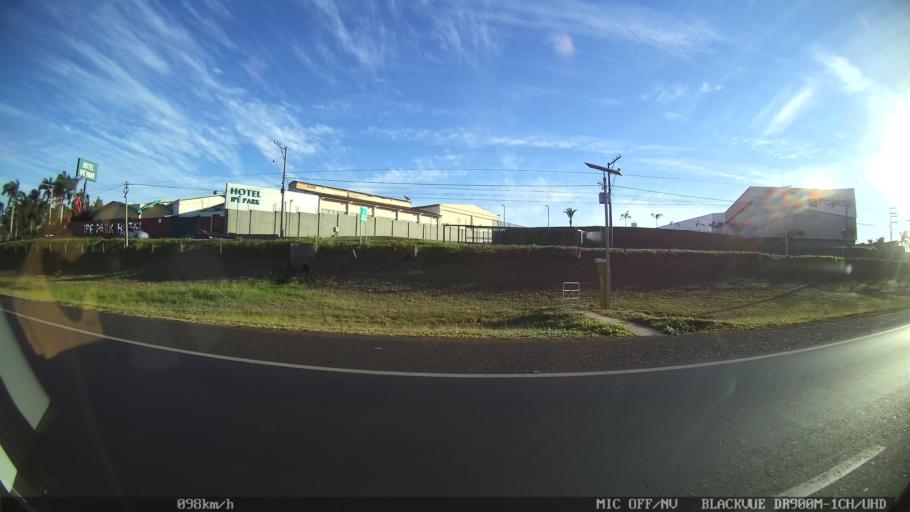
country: BR
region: Sao Paulo
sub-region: Sao Jose Do Rio Preto
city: Sao Jose do Rio Preto
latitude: -20.8869
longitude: -49.3116
